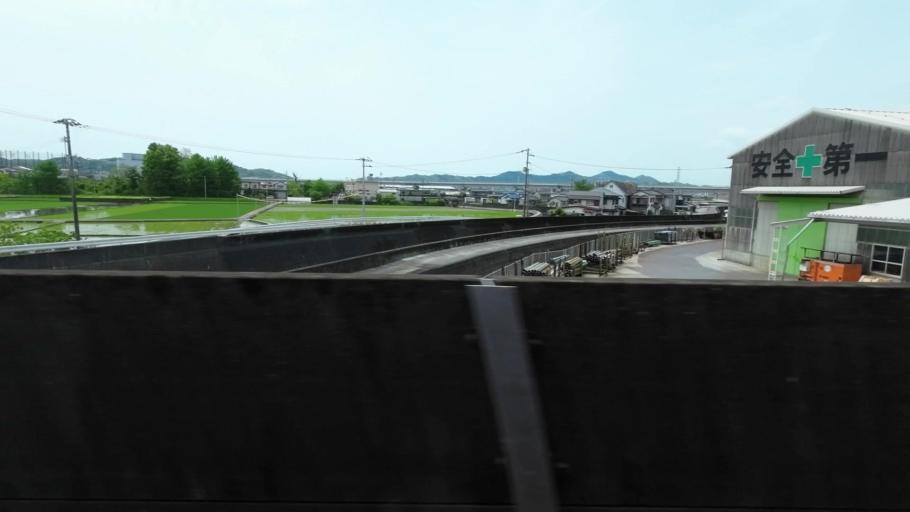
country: JP
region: Kochi
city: Kochi-shi
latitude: 33.5808
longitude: 133.5731
